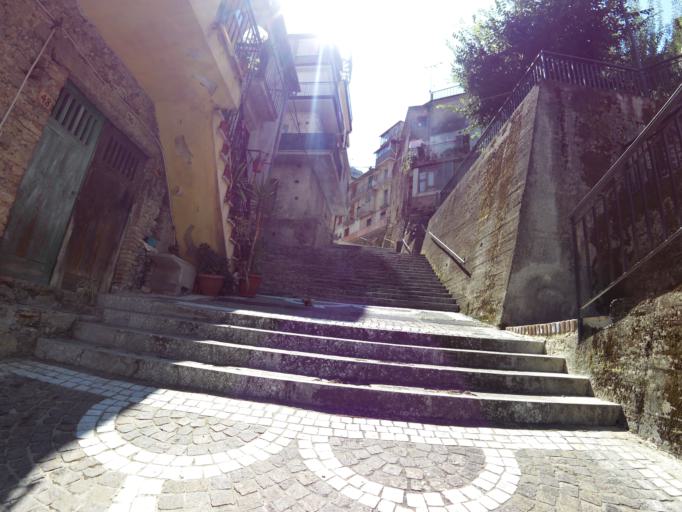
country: IT
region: Calabria
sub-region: Provincia di Reggio Calabria
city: Bivongi
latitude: 38.4822
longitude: 16.4534
